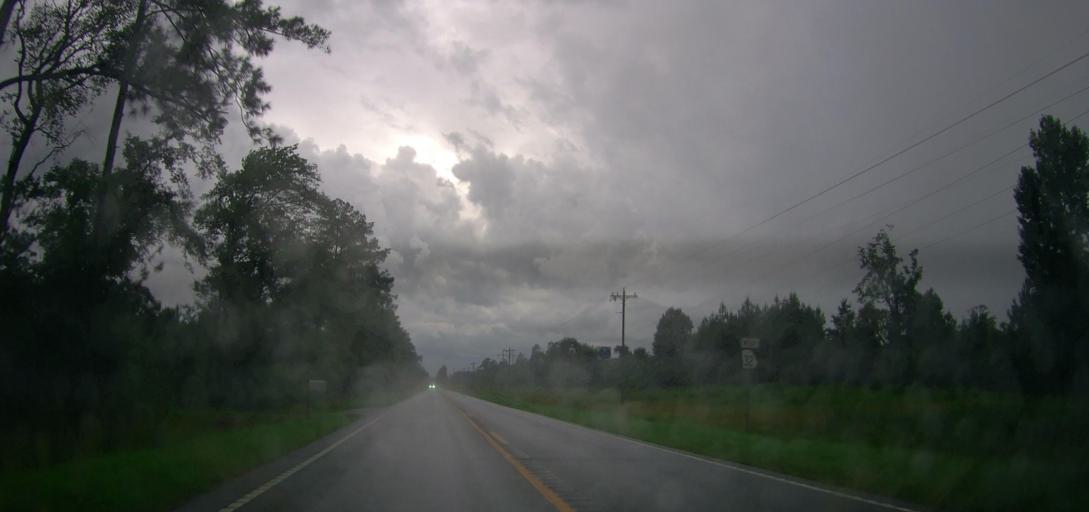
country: US
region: Georgia
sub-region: Brantley County
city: Nahunta
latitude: 31.3334
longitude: -81.9012
